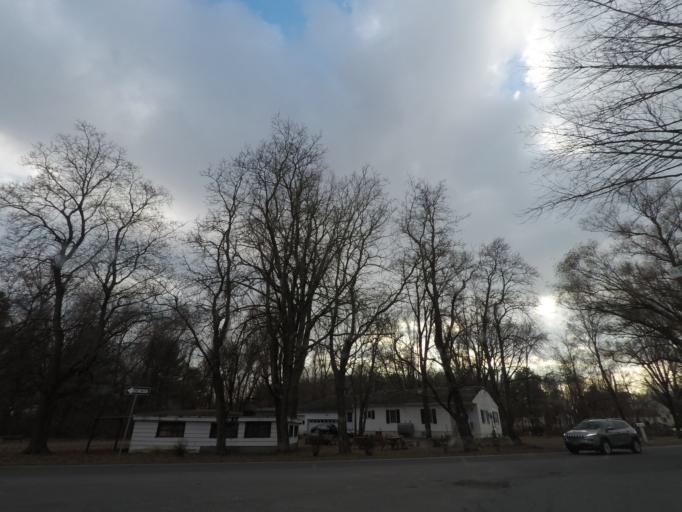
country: US
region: New York
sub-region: Albany County
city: McKownville
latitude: 42.6961
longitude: -73.8520
